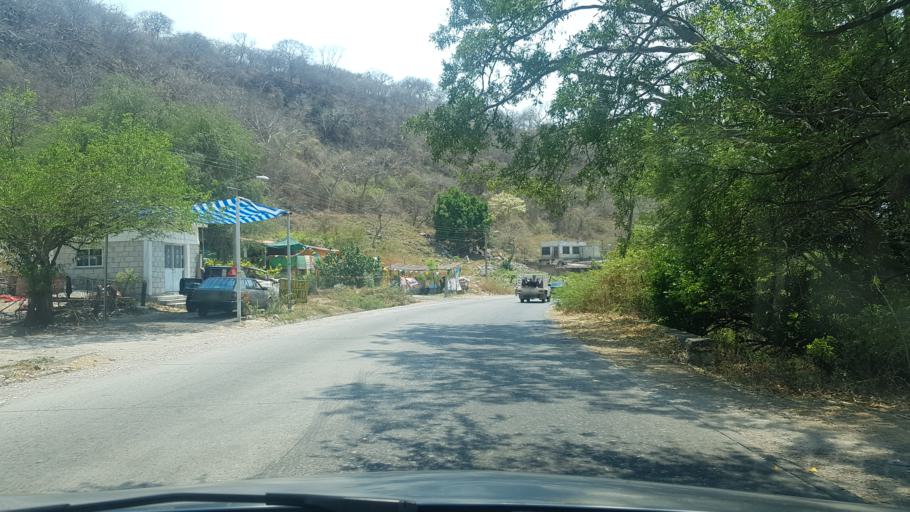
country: MX
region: Morelos
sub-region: Jiutepec
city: Independencia
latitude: 18.8014
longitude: -99.0976
